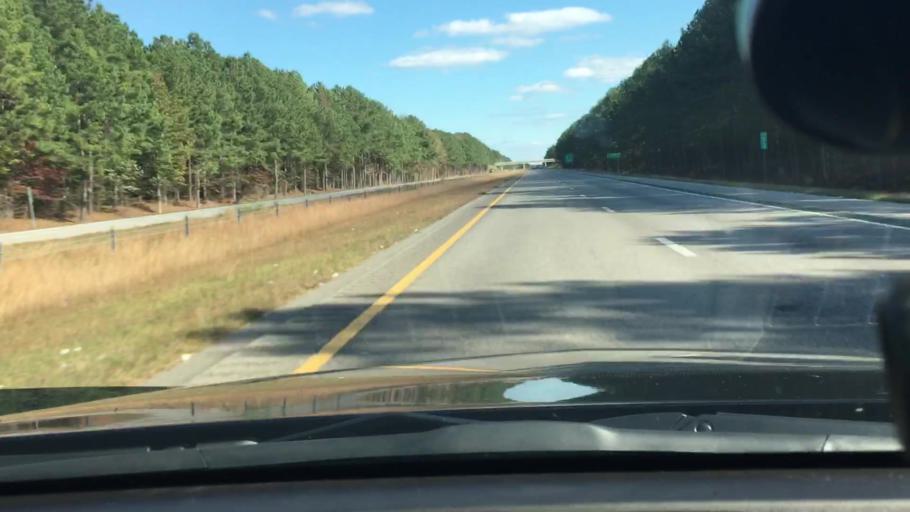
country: US
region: North Carolina
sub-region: Wilson County
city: Wilson
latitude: 35.6722
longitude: -77.7911
